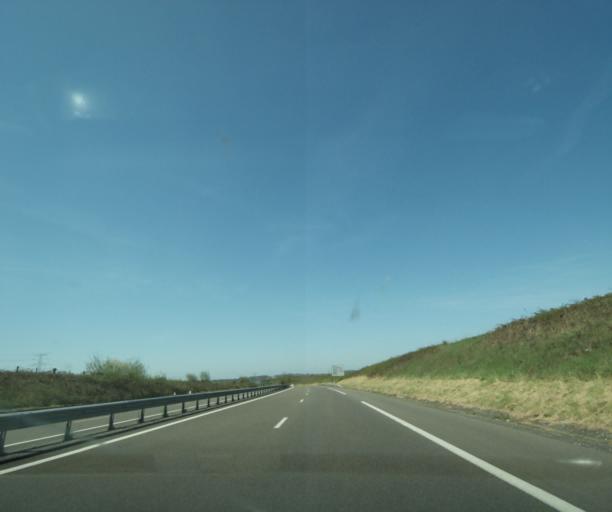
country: FR
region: Bourgogne
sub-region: Departement de la Nievre
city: Coulanges-les-Nevers
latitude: 47.0238
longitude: 3.1858
